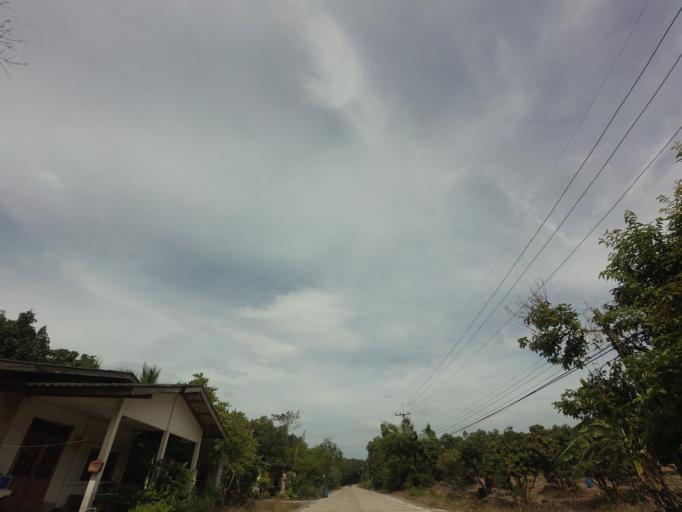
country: TH
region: Rayong
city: Klaeng
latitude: 12.6555
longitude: 101.5616
